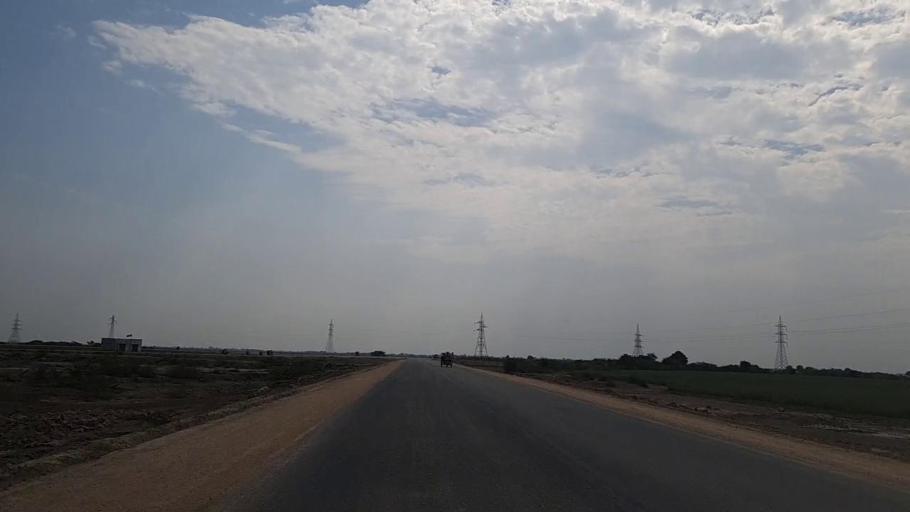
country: PK
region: Sindh
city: Naukot
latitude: 24.9566
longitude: 69.2828
